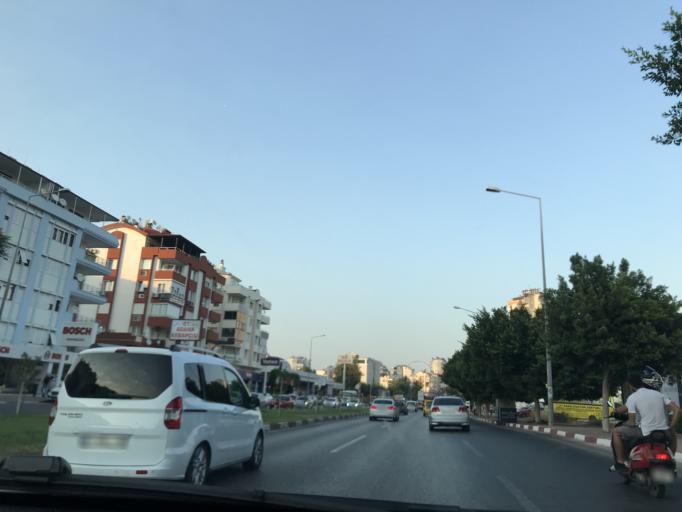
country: TR
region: Antalya
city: Antalya
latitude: 36.8778
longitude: 30.6470
